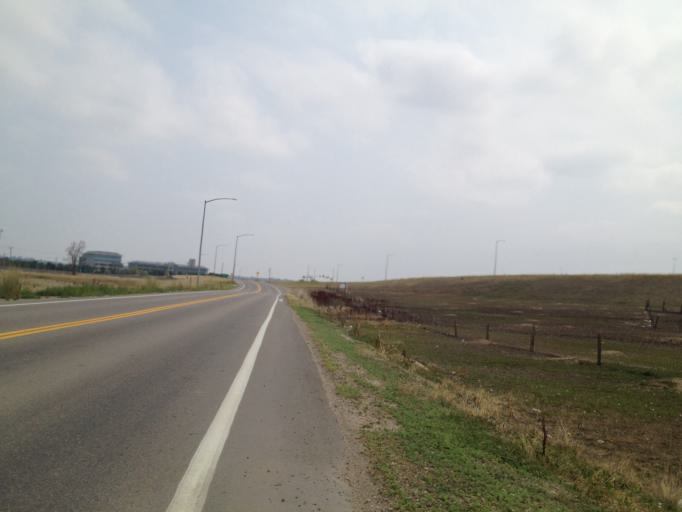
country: US
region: Colorado
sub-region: Broomfield County
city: Broomfield
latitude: 39.9032
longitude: -105.0802
